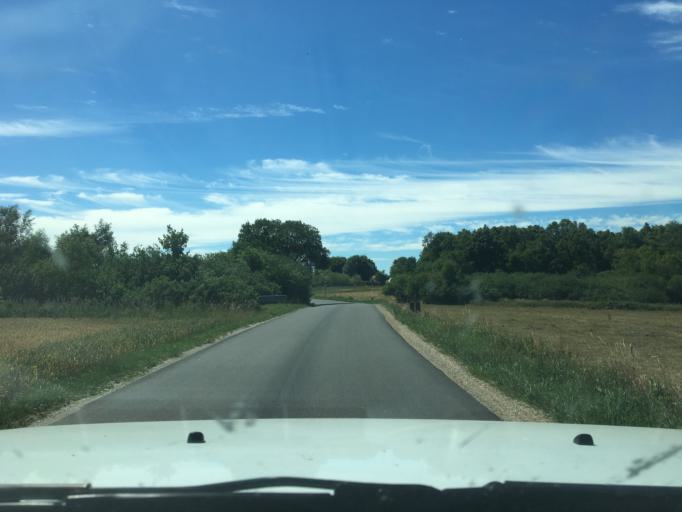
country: DK
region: Central Jutland
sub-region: Syddjurs Kommune
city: Ryomgard
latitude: 56.4322
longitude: 10.5683
